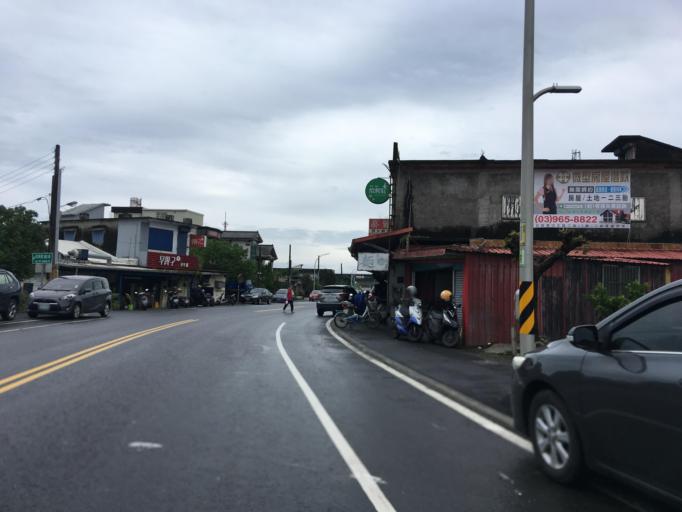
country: TW
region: Taiwan
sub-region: Yilan
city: Yilan
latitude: 24.6403
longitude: 121.8018
